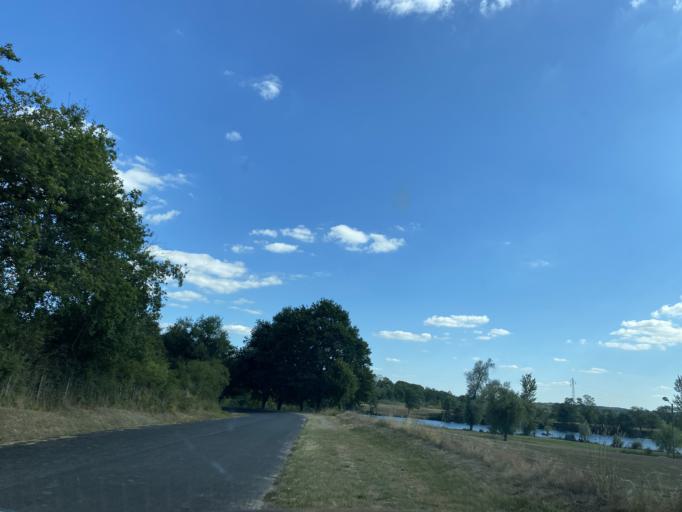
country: FR
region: Auvergne
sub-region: Departement du Puy-de-Dome
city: Peschadoires
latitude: 45.8704
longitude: 3.4876
